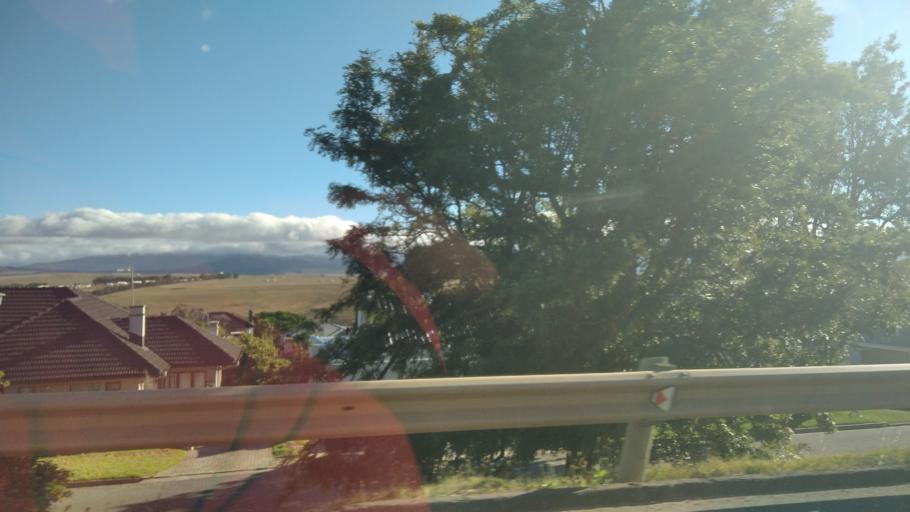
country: ZA
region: Western Cape
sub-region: Overberg District Municipality
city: Caledon
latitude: -34.2265
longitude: 19.4196
